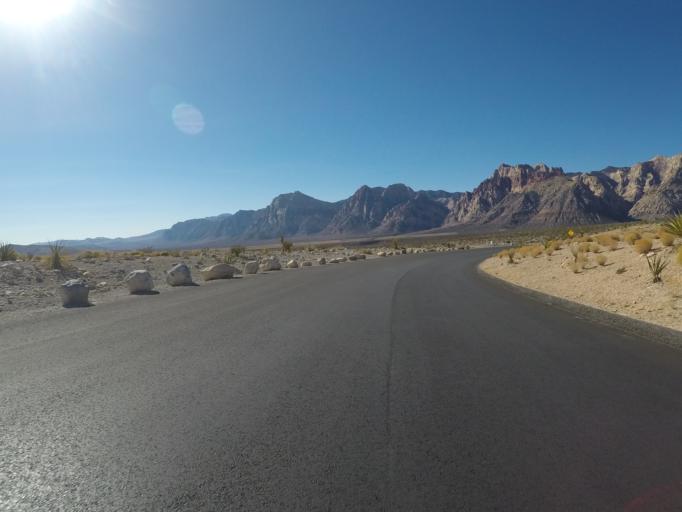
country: US
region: Nevada
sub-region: Clark County
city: Summerlin South
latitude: 36.1590
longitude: -115.4510
